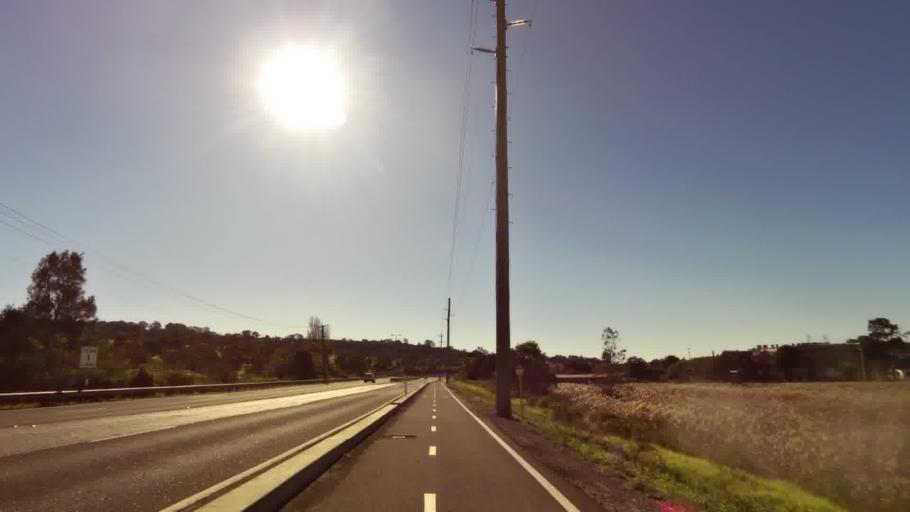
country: AU
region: New South Wales
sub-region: Wollongong
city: Koonawarra
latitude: -34.4724
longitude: 150.8159
